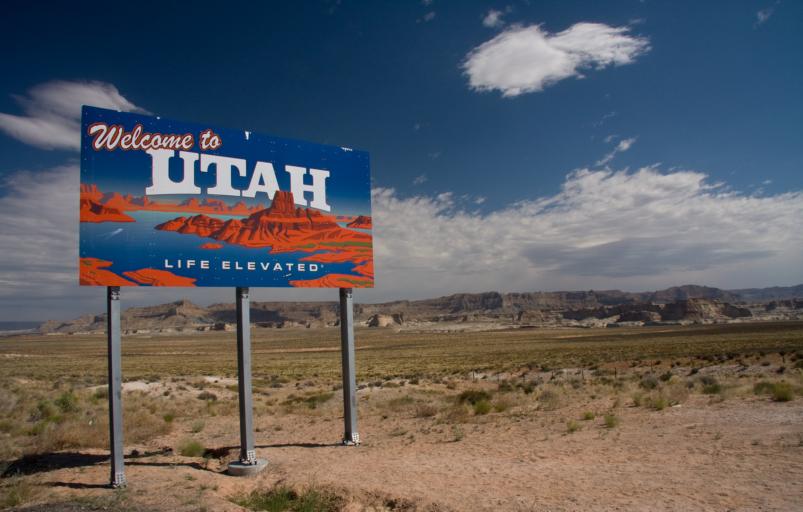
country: US
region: Arizona
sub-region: Coconino County
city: Page
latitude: 37.0020
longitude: -111.5729
